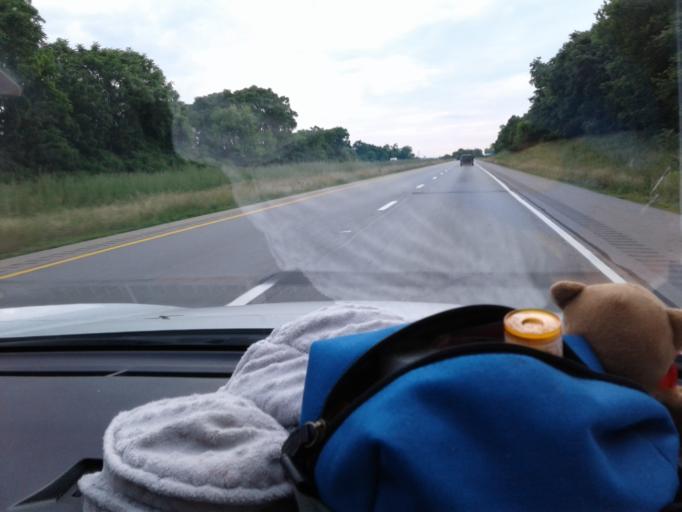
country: US
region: Pennsylvania
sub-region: Cumberland County
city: Newville
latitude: 40.1566
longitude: -77.2969
